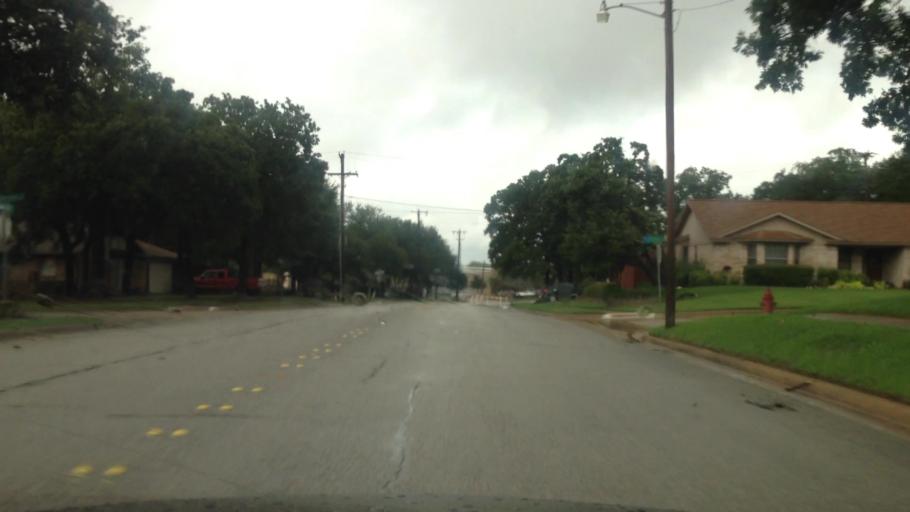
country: US
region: Texas
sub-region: Tarrant County
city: Colleyville
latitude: 32.8828
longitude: -97.2074
